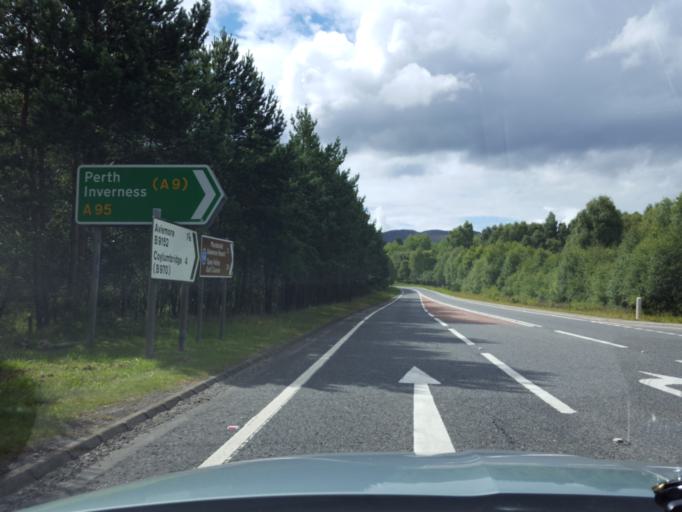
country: GB
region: Scotland
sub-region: Highland
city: Aviemore
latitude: 57.2144
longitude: -3.8195
